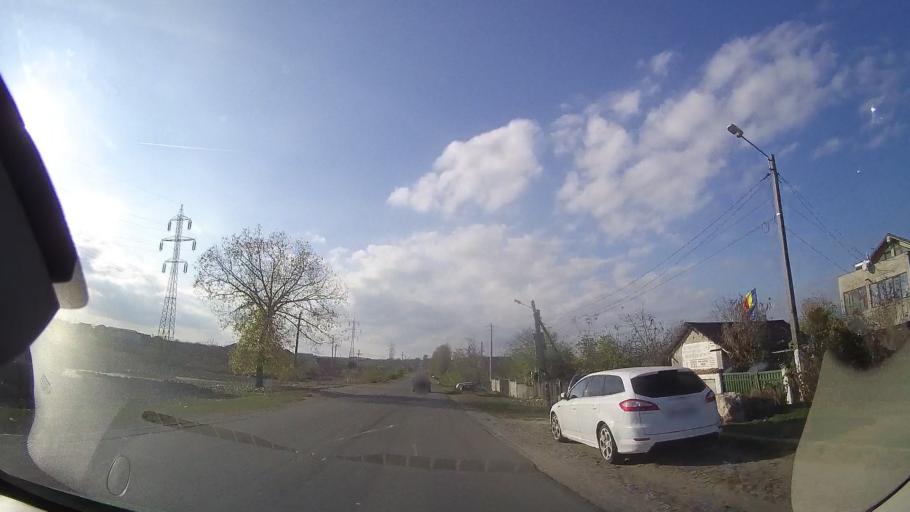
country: RO
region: Constanta
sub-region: Comuna Limanu
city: Limanu
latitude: 43.7937
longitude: 28.5410
